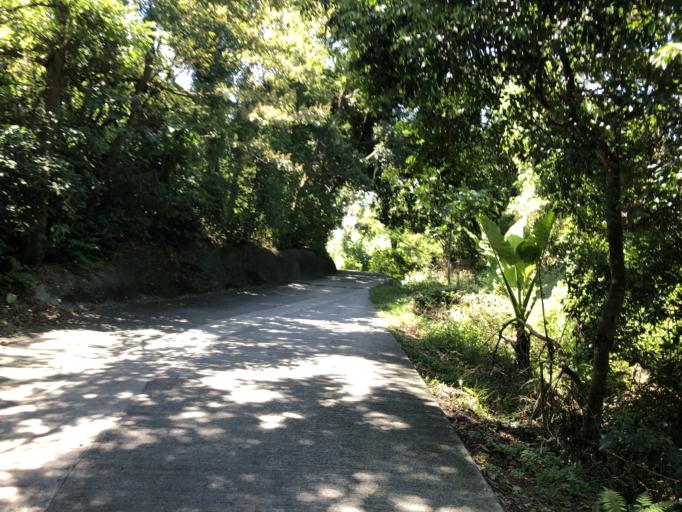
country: HK
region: Tuen Mun
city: Tuen Mun
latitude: 22.2950
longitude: 113.9725
